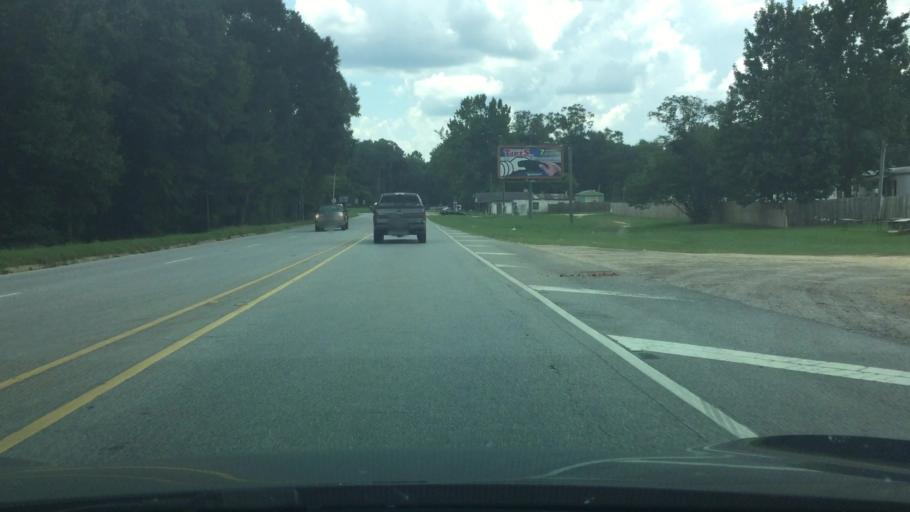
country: US
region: Alabama
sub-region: Pike County
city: Troy
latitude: 31.7559
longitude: -85.9606
